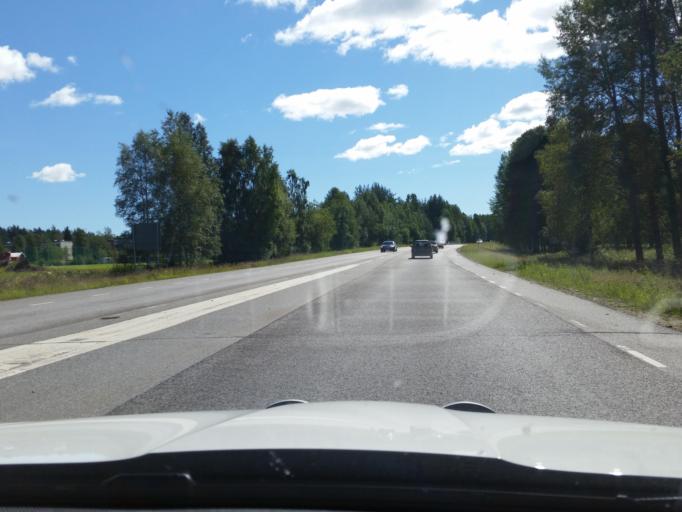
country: SE
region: Norrbotten
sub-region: Pitea Kommun
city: Pitea
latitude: 65.3091
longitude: 21.4997
